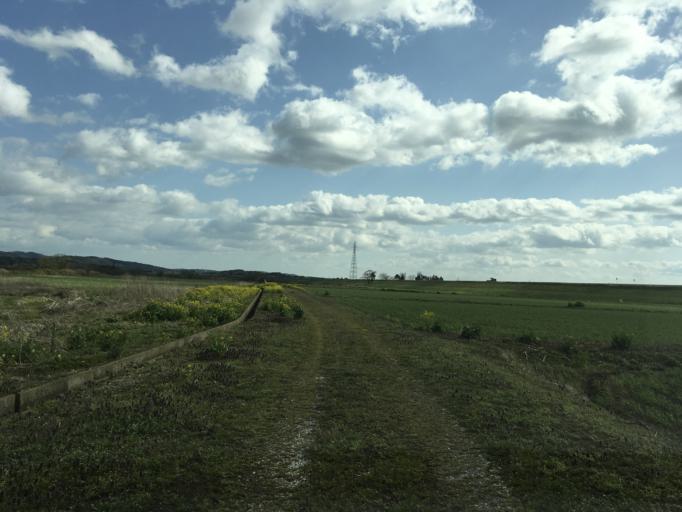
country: JP
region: Miyagi
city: Wakuya
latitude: 38.7225
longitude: 141.2656
